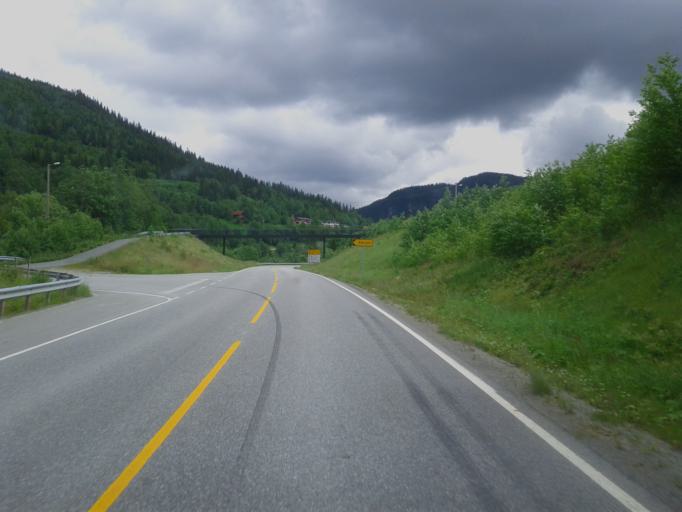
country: NO
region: Sor-Trondelag
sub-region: Midtre Gauldal
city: Storen
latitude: 62.9424
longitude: 10.6480
